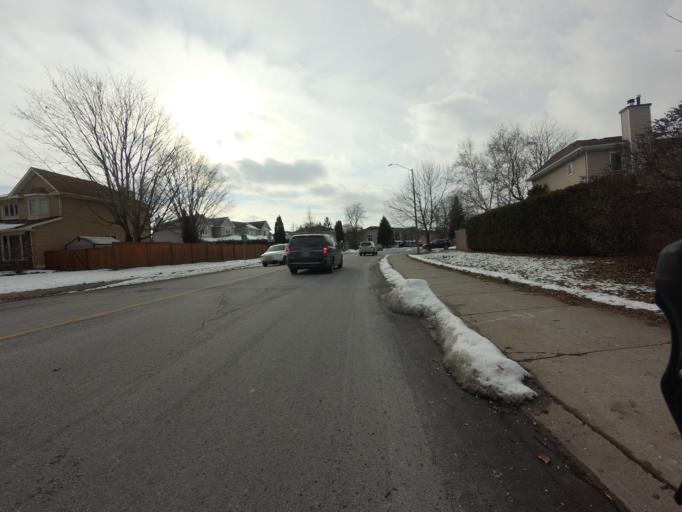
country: CA
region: Ontario
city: Bells Corners
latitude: 45.2726
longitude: -75.7653
